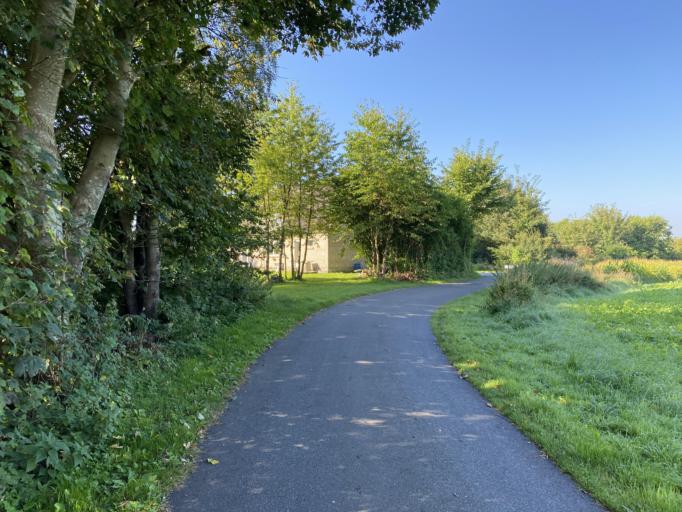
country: DK
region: South Denmark
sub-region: Nyborg Kommune
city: Nyborg
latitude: 55.2386
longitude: 10.7050
